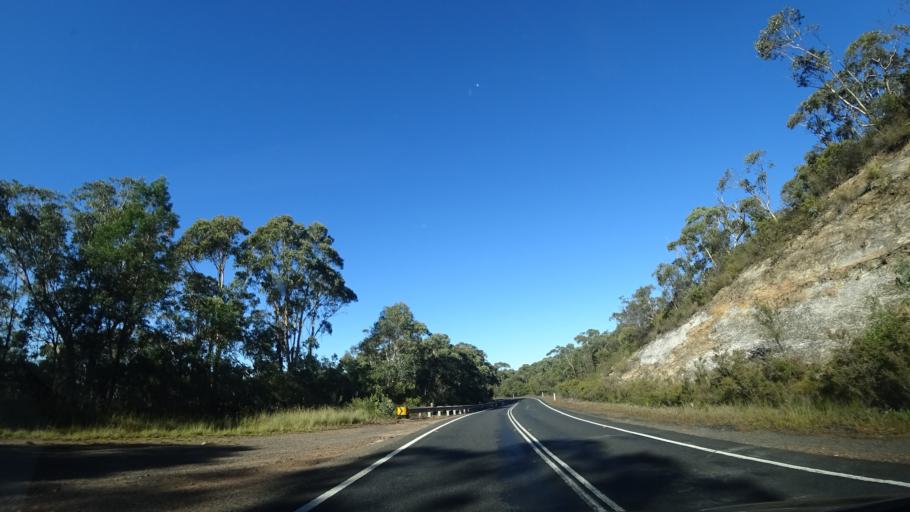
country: AU
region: New South Wales
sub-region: Blue Mountains Municipality
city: Blackheath
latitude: -33.5466
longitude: 150.3848
